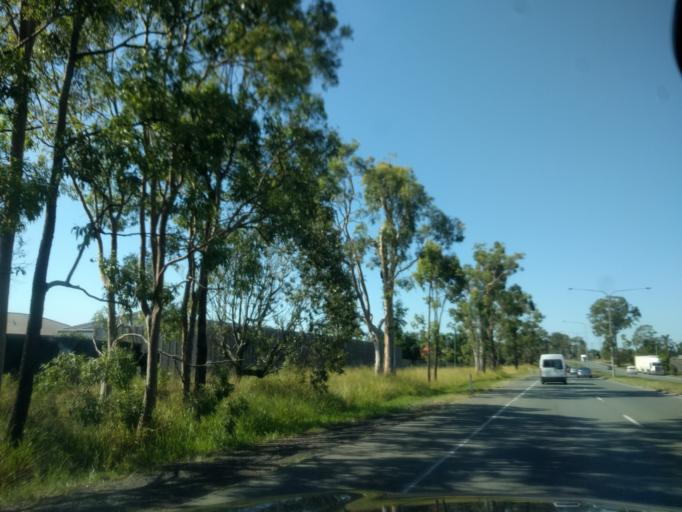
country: AU
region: Queensland
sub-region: Brisbane
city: Sunnybank Hills
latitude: -27.6357
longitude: 153.0455
